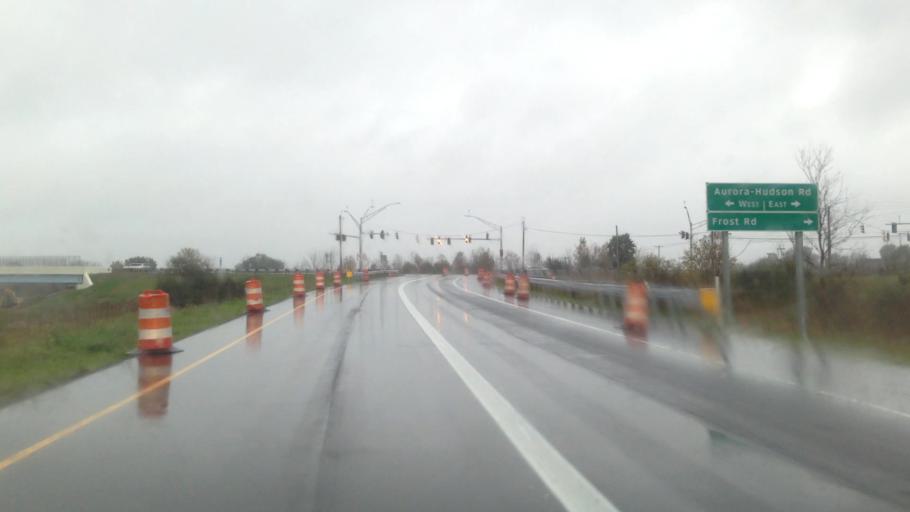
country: US
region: Ohio
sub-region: Portage County
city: Streetsboro
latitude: 41.2604
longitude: -81.3755
